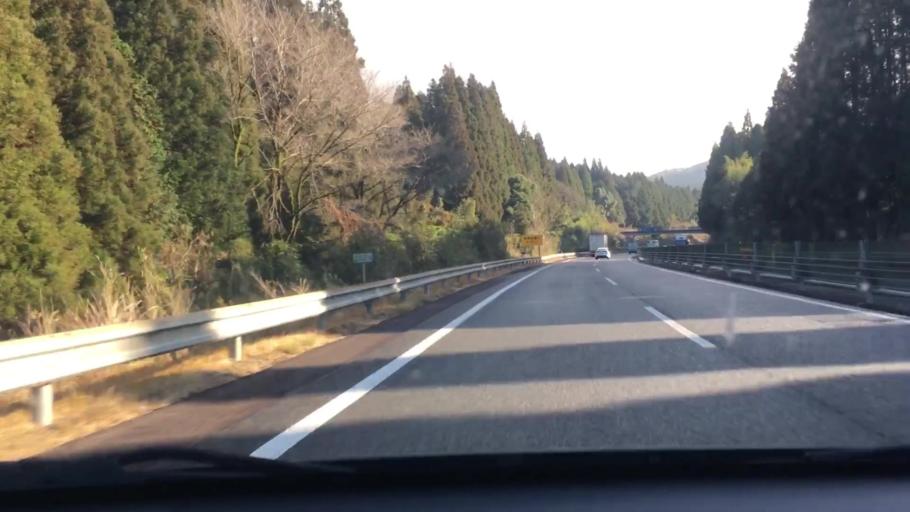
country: JP
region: Kagoshima
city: Okuchi-shinohara
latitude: 32.0004
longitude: 130.7580
